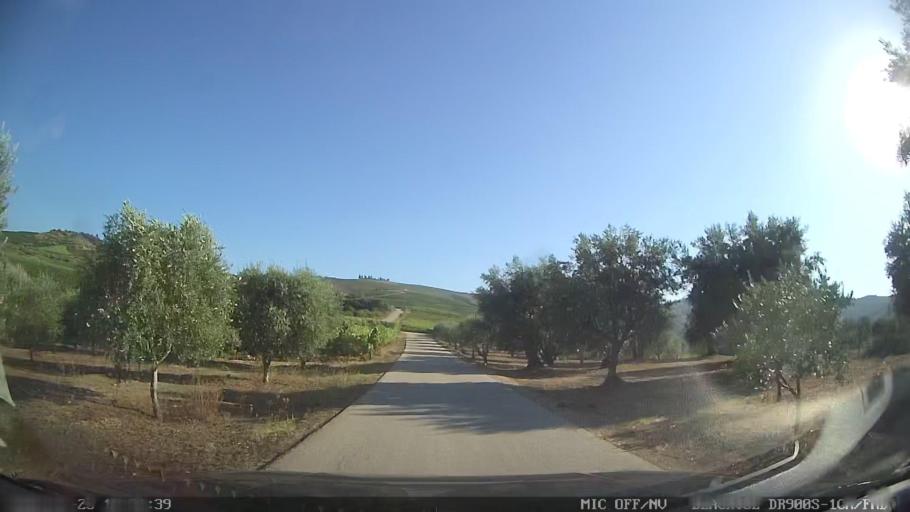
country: PT
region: Viseu
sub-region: Sao Joao da Pesqueira
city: Sao Joao da Pesqueira
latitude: 41.1767
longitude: -7.4060
